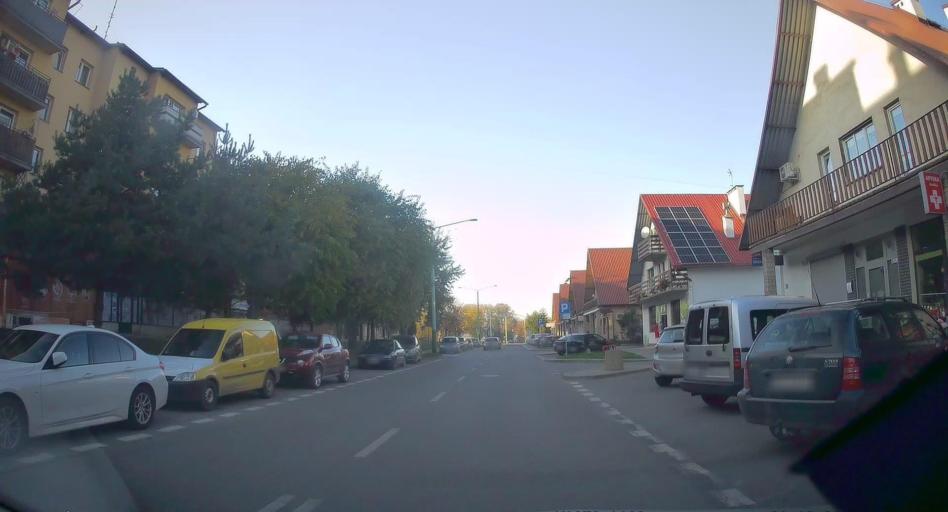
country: PL
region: Subcarpathian Voivodeship
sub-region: Powiat debicki
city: Debica
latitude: 50.0575
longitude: 21.4024
